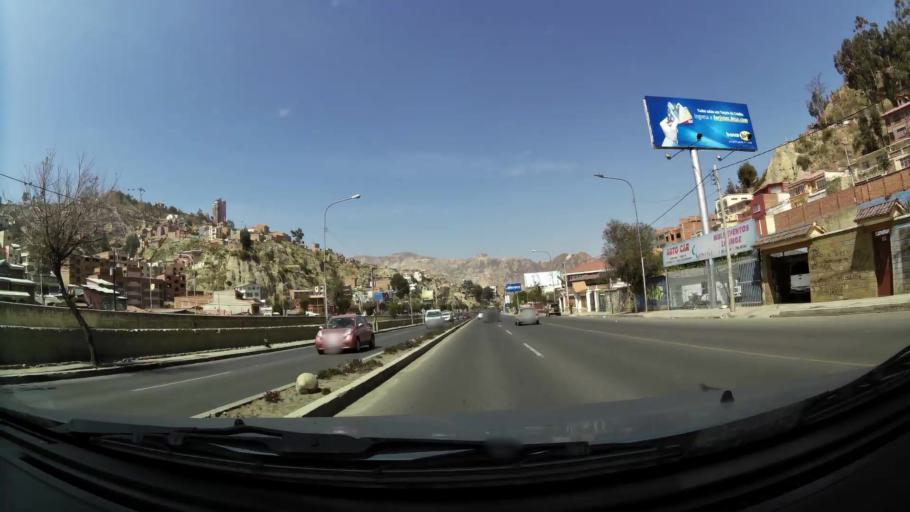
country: BO
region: La Paz
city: La Paz
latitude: -16.5332
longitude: -68.0982
